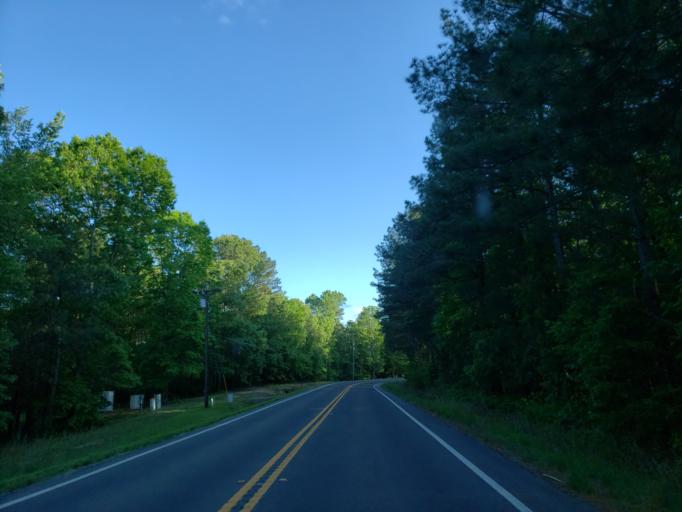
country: US
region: Georgia
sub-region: Cherokee County
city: Canton
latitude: 34.2538
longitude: -84.6009
